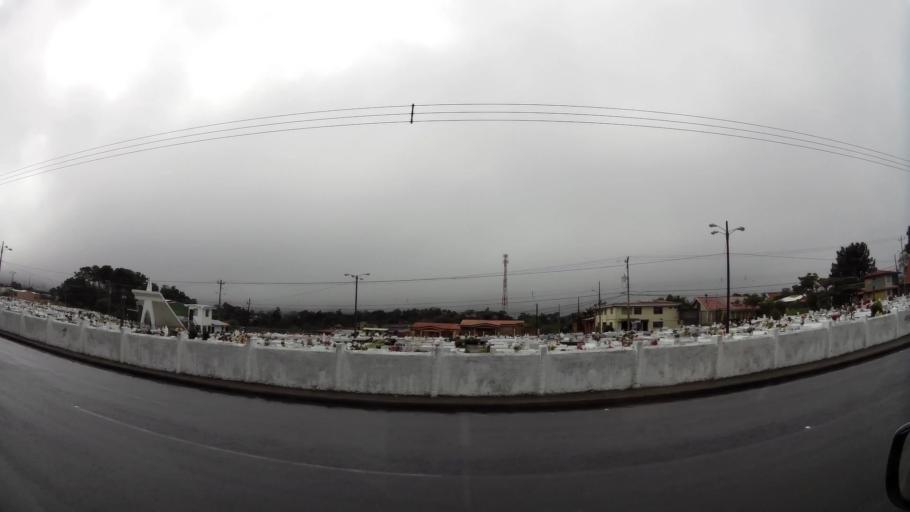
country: CR
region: Cartago
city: Paraiso
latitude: 9.8399
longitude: -83.8743
